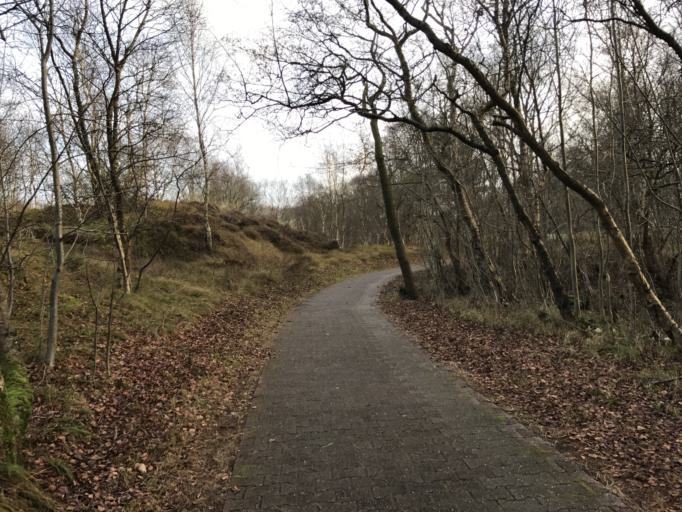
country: DE
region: Lower Saxony
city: Borkum
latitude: 53.5766
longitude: 6.6964
